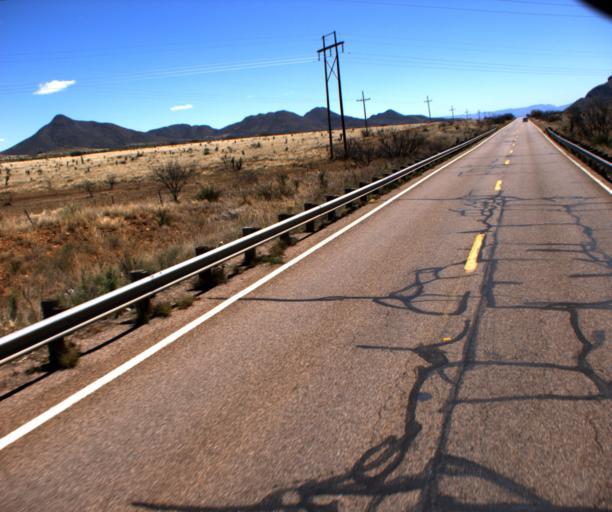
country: US
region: Arizona
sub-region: Cochise County
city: Huachuca City
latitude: 31.7218
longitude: -110.4813
